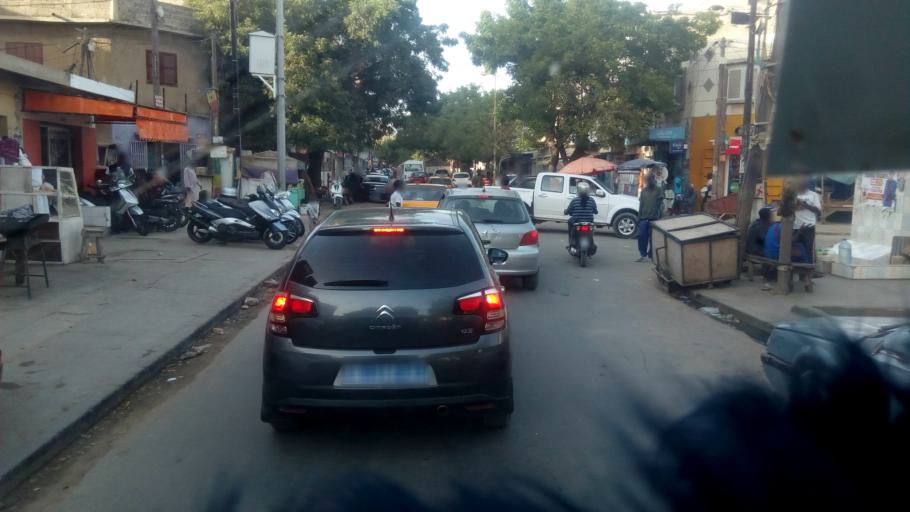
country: SN
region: Dakar
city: Grand Dakar
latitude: 14.7117
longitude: -17.4497
